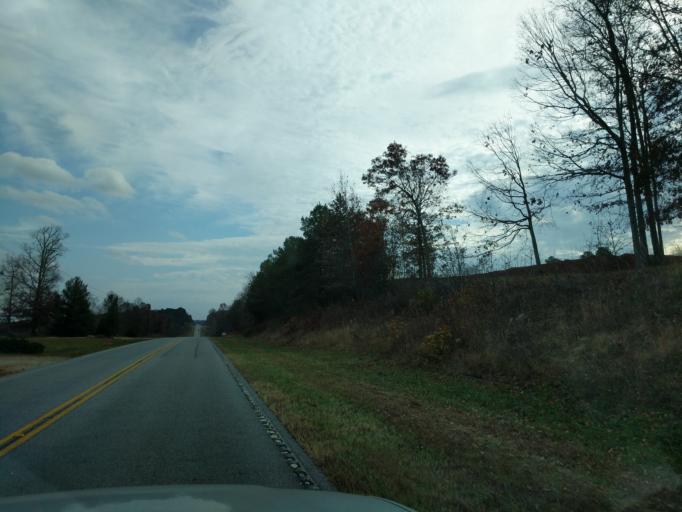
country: US
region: Georgia
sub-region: Franklin County
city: Gumlog
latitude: 34.5191
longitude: -83.0481
